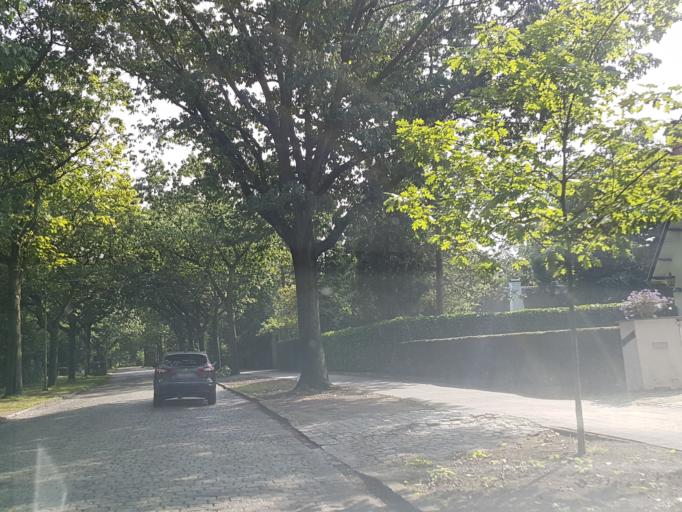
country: BE
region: Flanders
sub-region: Provincie Antwerpen
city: Brasschaat
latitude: 51.2739
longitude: 4.4643
